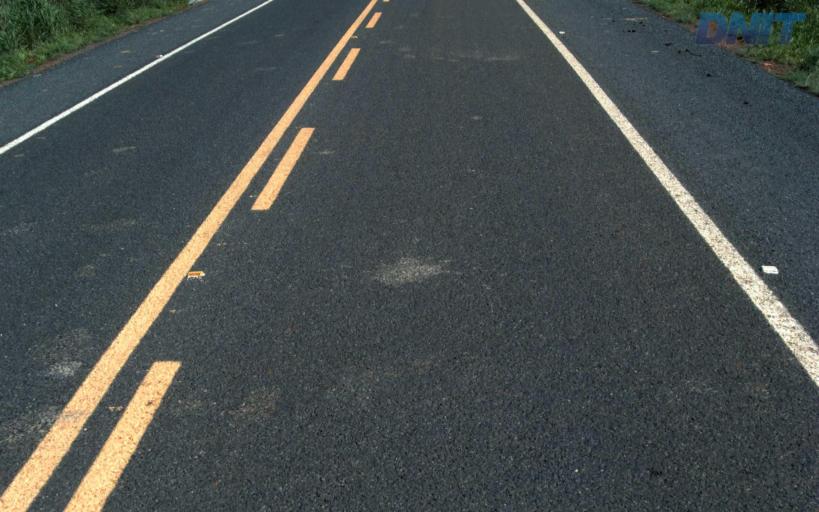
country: BR
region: Goias
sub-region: Sao Miguel Do Araguaia
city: Sao Miguel do Araguaia
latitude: -13.3478
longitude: -50.1502
